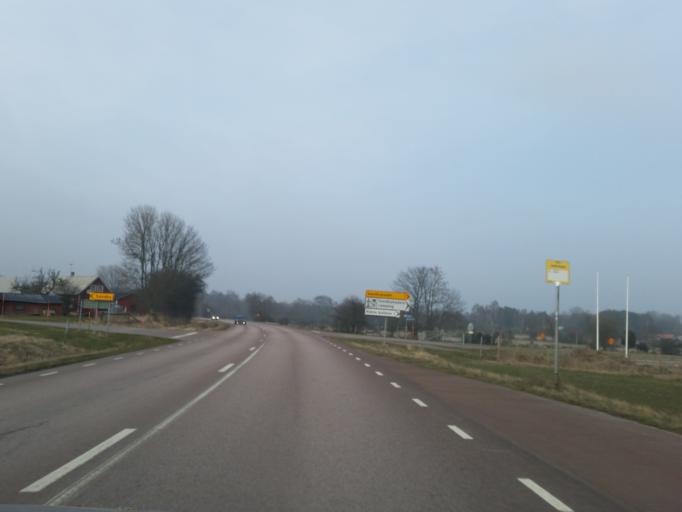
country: SE
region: Kalmar
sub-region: Borgholms Kommun
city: Borgholm
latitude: 57.1726
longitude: 17.0250
